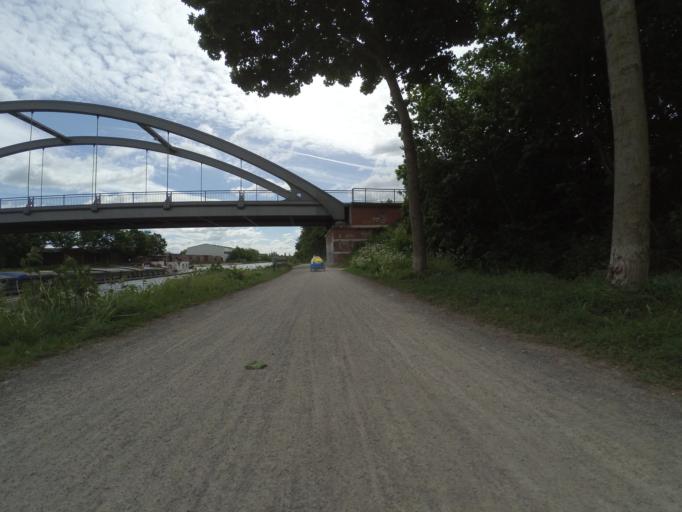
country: DE
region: Lower Saxony
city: Langenhagen
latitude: 52.4156
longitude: 9.7160
